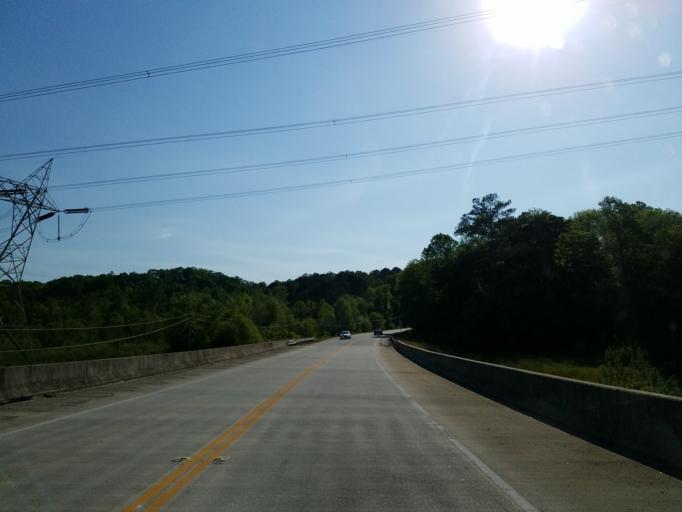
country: US
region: Georgia
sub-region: Paulding County
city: Dallas
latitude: 33.8669
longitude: -84.8915
